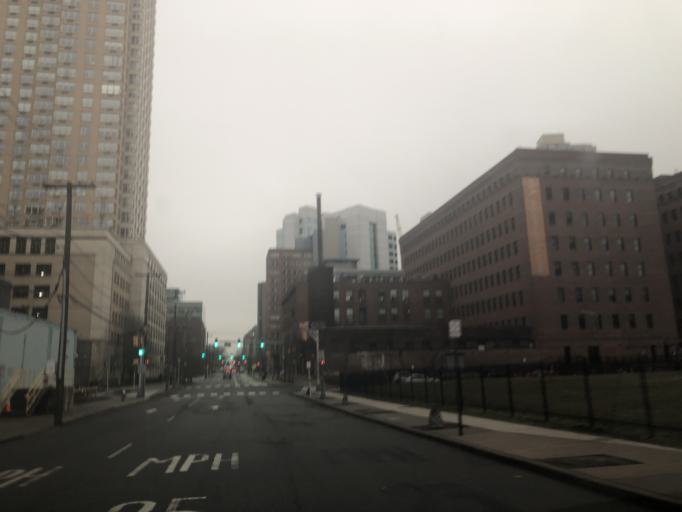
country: US
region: New Jersey
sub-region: Hudson County
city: Hoboken
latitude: 40.7208
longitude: -74.0365
